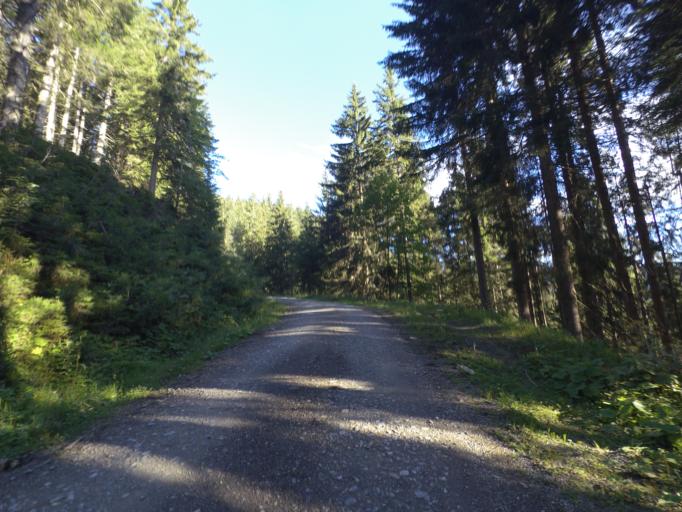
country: AT
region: Salzburg
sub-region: Politischer Bezirk Sankt Johann im Pongau
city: Goldegg
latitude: 47.3466
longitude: 13.1070
